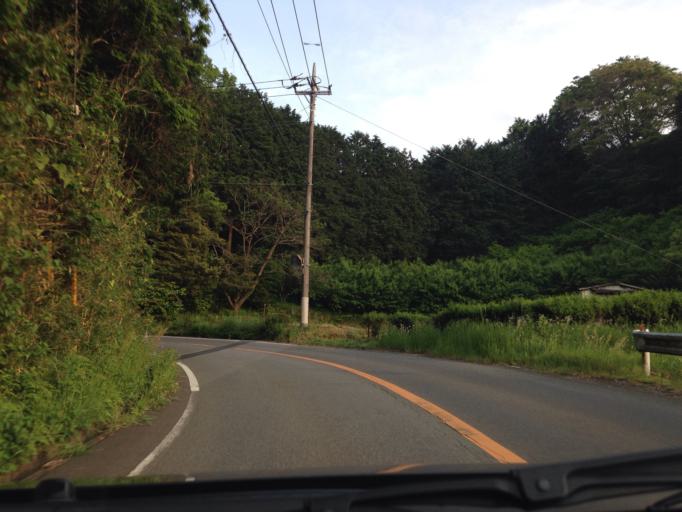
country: JP
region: Shizuoka
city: Mishima
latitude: 35.1661
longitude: 138.9259
